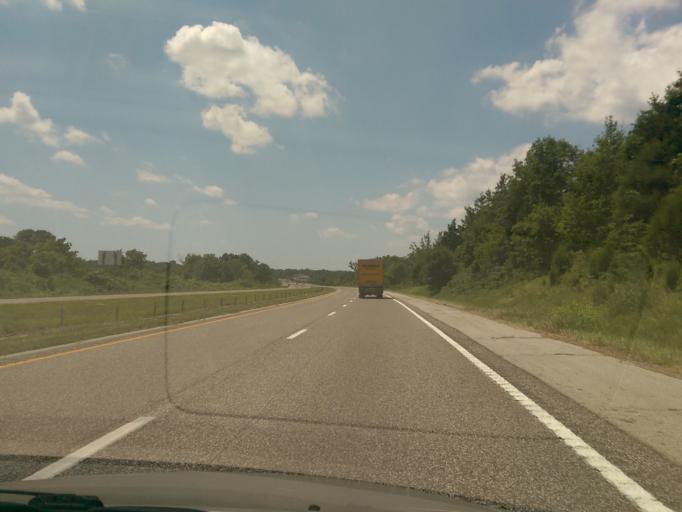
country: US
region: Missouri
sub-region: Boone County
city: Columbia
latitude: 38.9730
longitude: -92.5218
